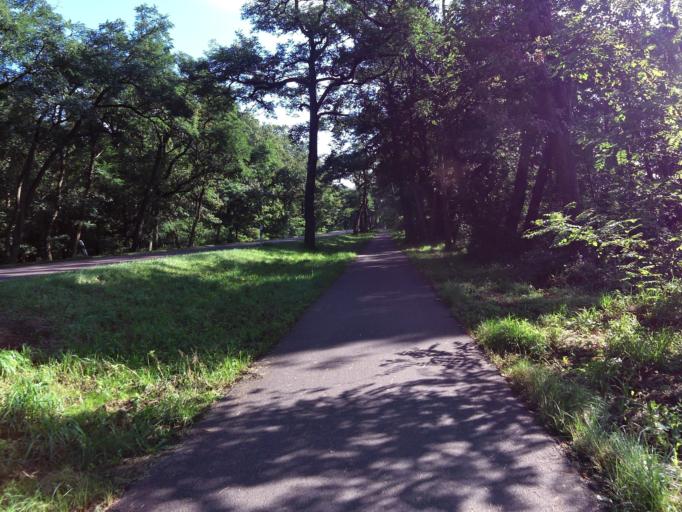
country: DE
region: Saxony-Anhalt
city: Coswig
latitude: 51.8814
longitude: 12.4890
